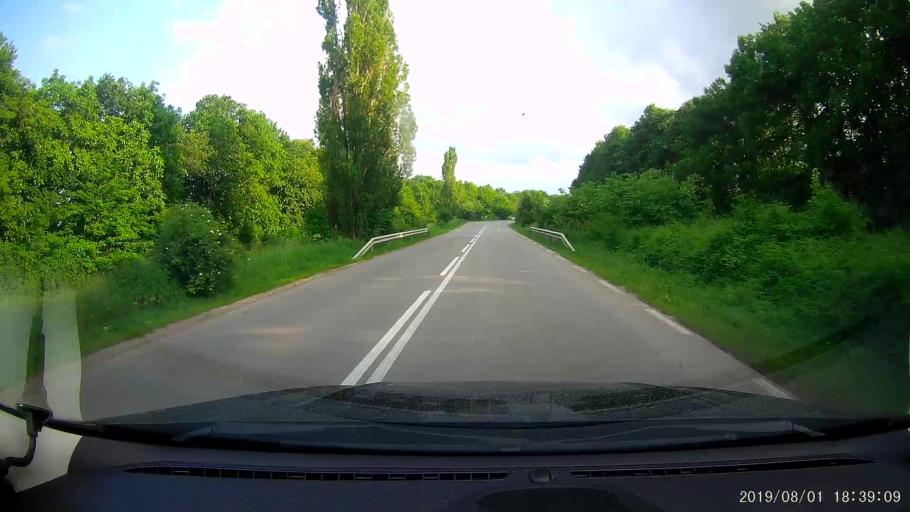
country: BG
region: Shumen
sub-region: Obshtina Khitrino
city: Gara Khitrino
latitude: 43.3914
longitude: 26.9173
